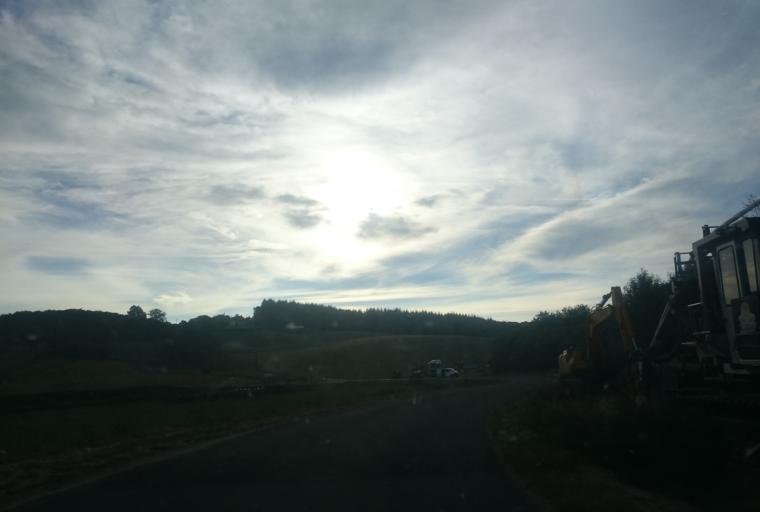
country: FR
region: Auvergne
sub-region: Departement du Cantal
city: Laroquebrou
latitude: 44.9333
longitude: 2.1944
